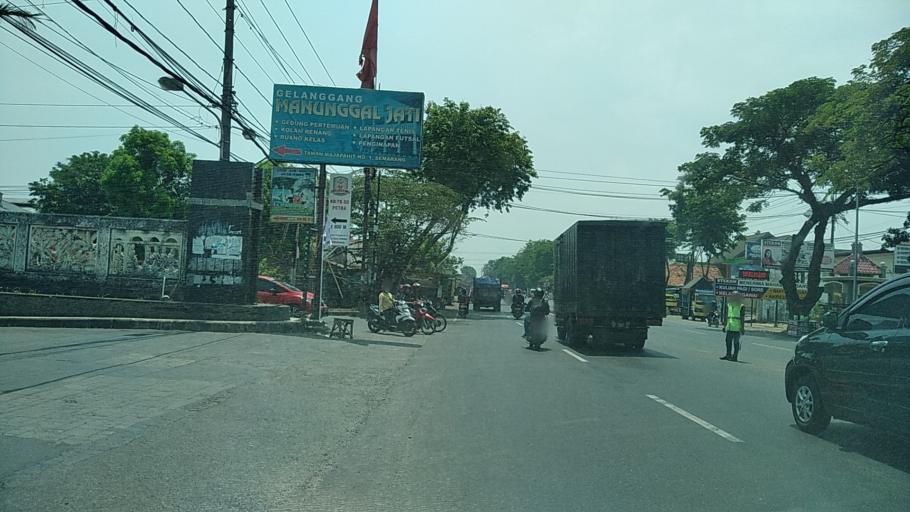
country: ID
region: Central Java
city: Mranggen
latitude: -7.0145
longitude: 110.4815
